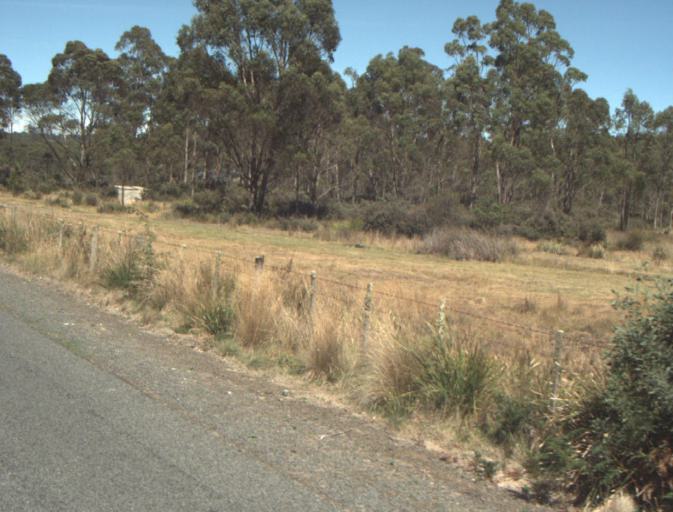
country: AU
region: Tasmania
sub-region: Launceston
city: Newstead
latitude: -41.3722
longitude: 147.2978
